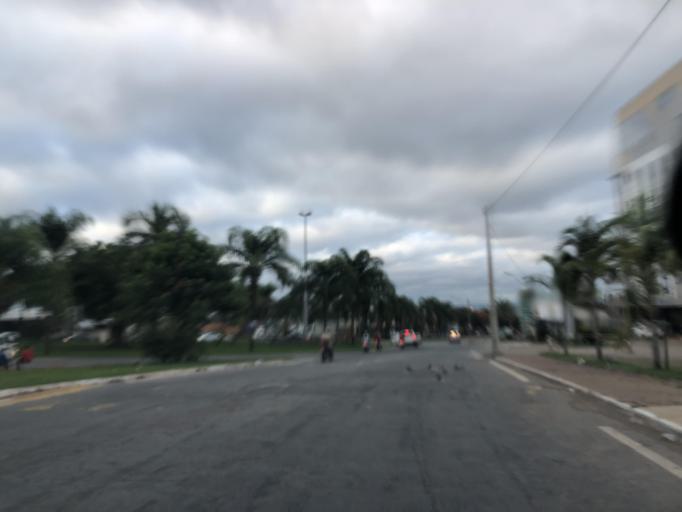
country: BR
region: Goias
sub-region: Goiania
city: Goiania
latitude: -16.6184
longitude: -49.2069
